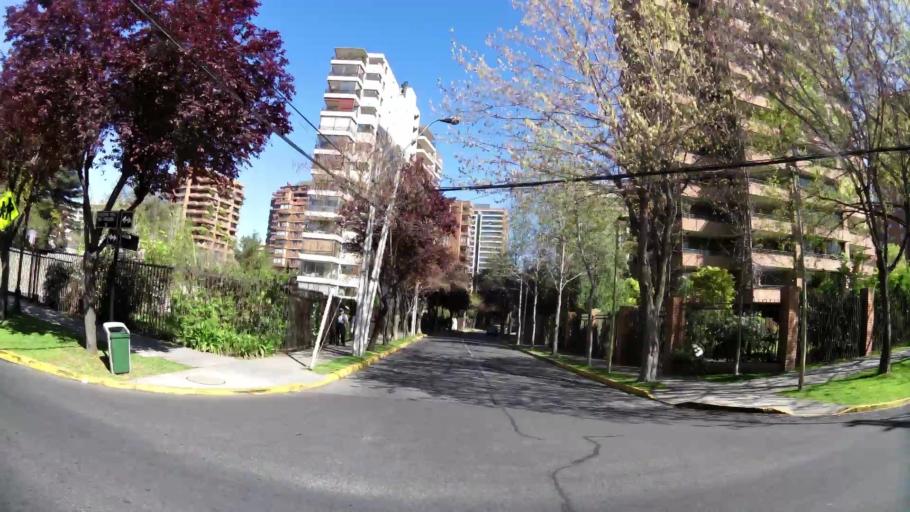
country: CL
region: Santiago Metropolitan
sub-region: Provincia de Santiago
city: Villa Presidente Frei, Nunoa, Santiago, Chile
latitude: -33.4048
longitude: -70.5611
